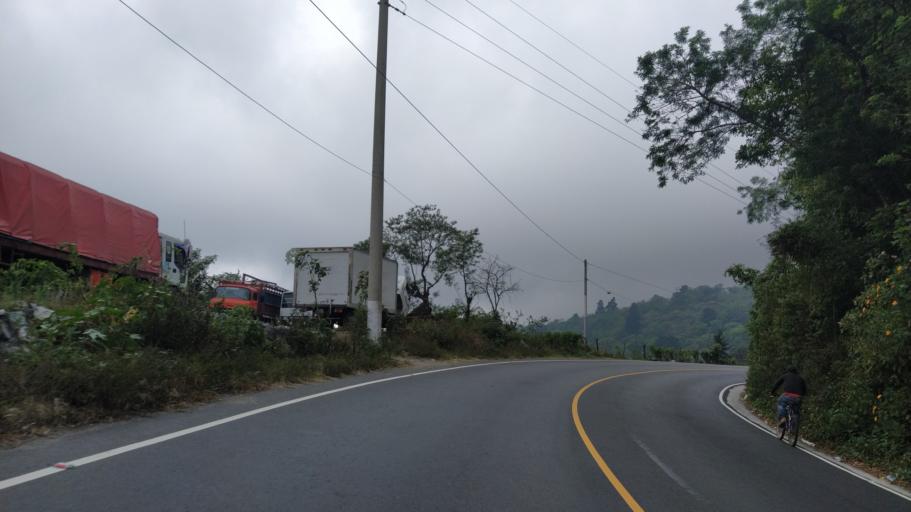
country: GT
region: Quetzaltenango
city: Zunil
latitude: 14.7270
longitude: -91.5252
